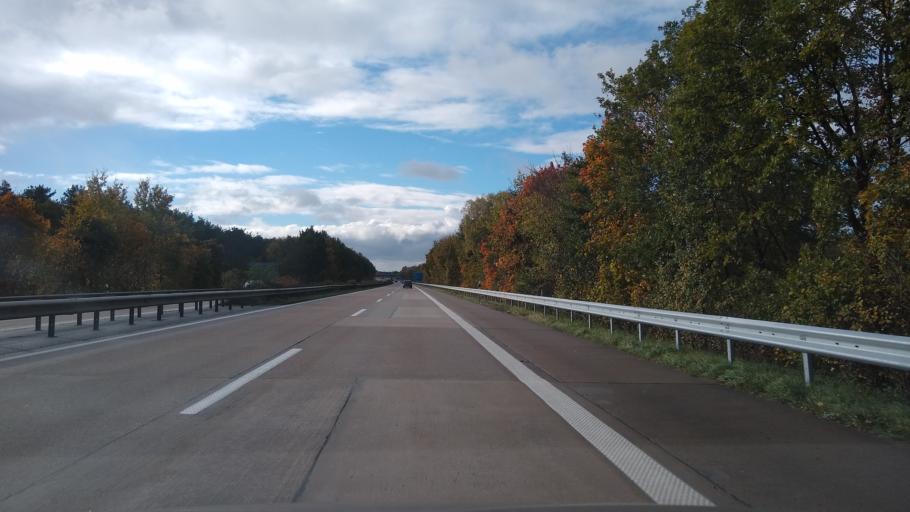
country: DE
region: Lower Saxony
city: Wardenburg
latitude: 53.0691
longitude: 8.2402
